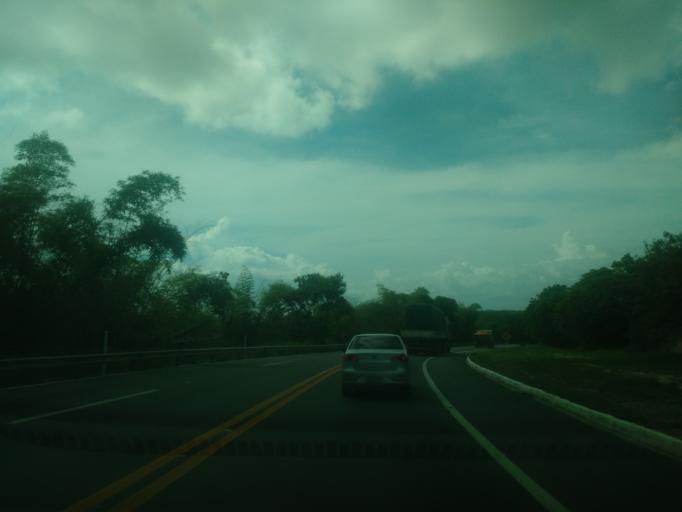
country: BR
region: Alagoas
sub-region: Marechal Deodoro
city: Marechal Deodoro
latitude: -9.6896
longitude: -35.8167
